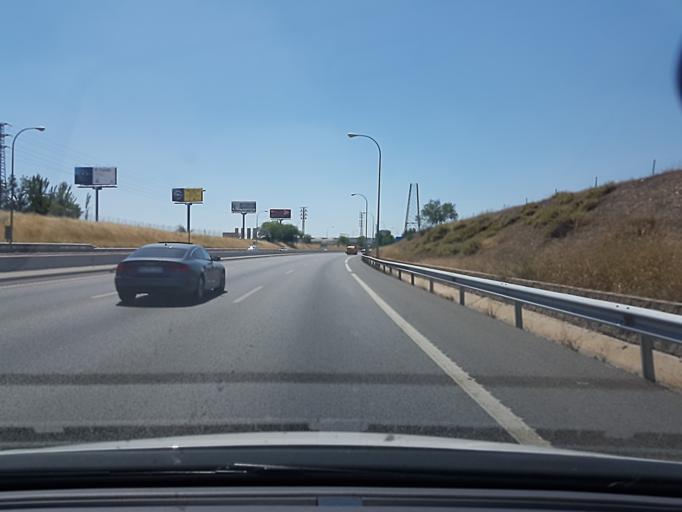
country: ES
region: Madrid
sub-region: Provincia de Madrid
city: Villaverde
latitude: 40.3640
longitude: -3.7006
